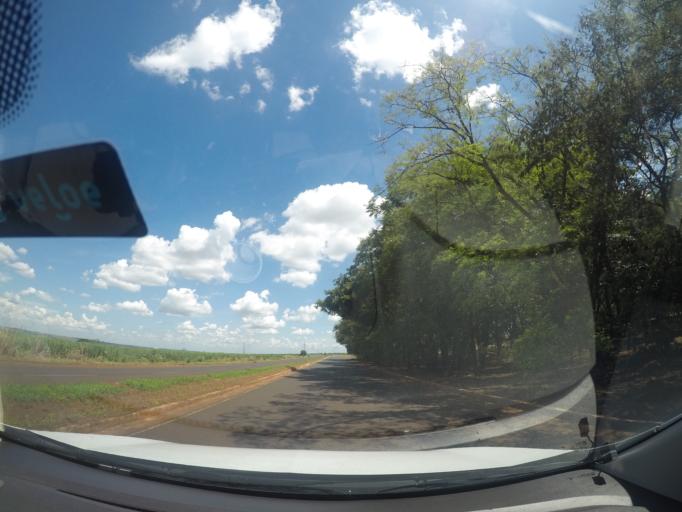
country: BR
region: Minas Gerais
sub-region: Frutal
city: Frutal
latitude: -19.8144
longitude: -48.7305
